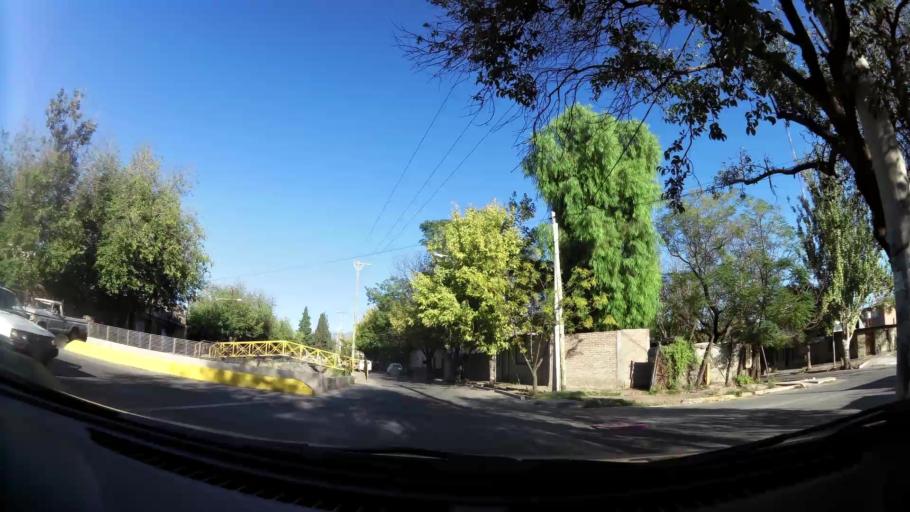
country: AR
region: Mendoza
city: Las Heras
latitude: -32.8617
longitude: -68.8308
